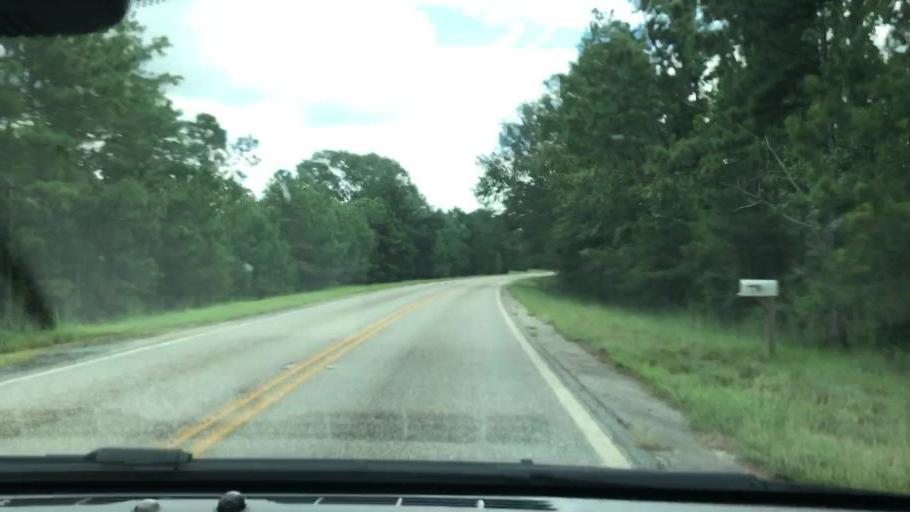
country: US
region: Georgia
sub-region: Stewart County
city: Lumpkin
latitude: 32.0703
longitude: -84.8440
